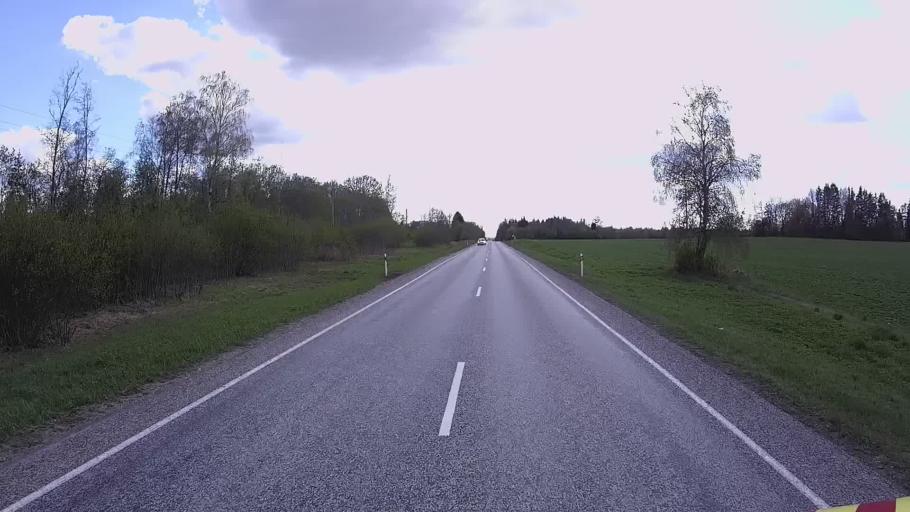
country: EE
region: Jogevamaa
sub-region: Jogeva linn
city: Jogeva
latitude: 58.7701
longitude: 26.4539
